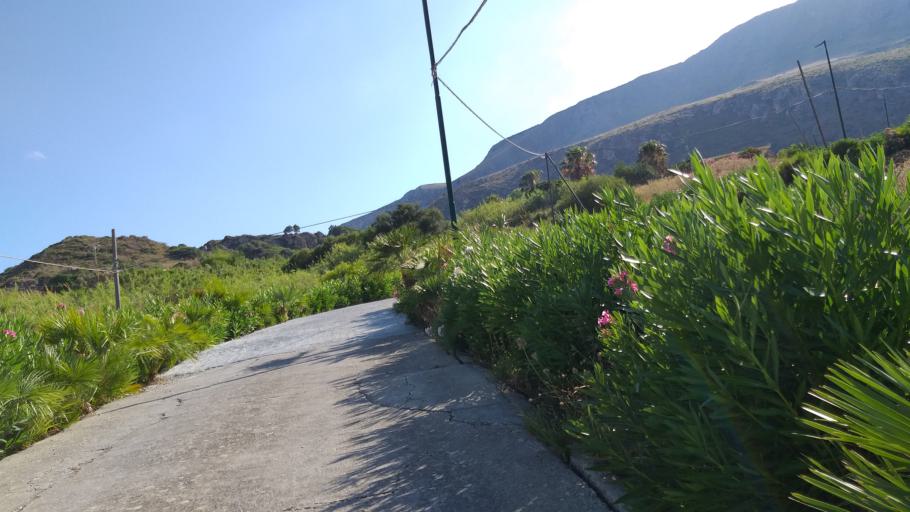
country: IT
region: Sicily
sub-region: Trapani
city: Castelluzzo
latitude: 38.0758
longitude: 12.8107
